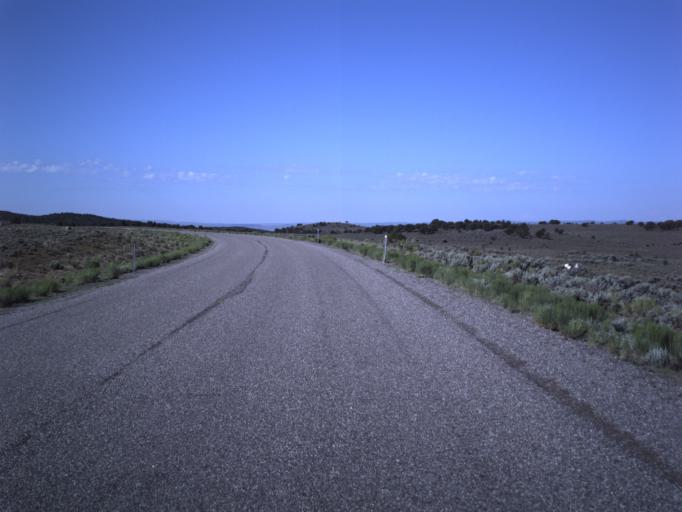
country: US
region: Utah
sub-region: Wayne County
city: Loa
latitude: 38.5035
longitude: -111.5317
